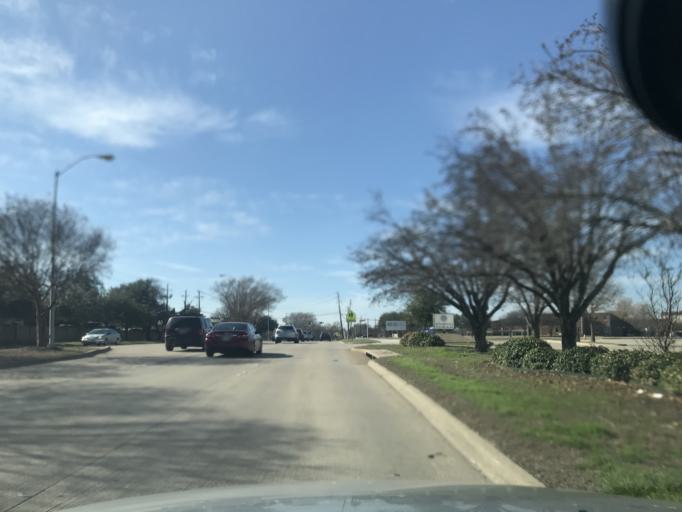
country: US
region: Texas
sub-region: Dallas County
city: Addison
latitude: 33.0426
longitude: -96.8101
